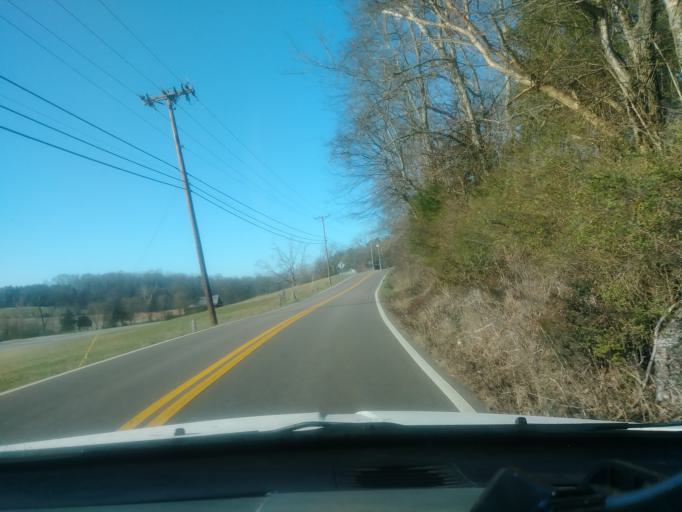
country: US
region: Tennessee
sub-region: Greene County
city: Mosheim
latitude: 36.1192
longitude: -82.9401
